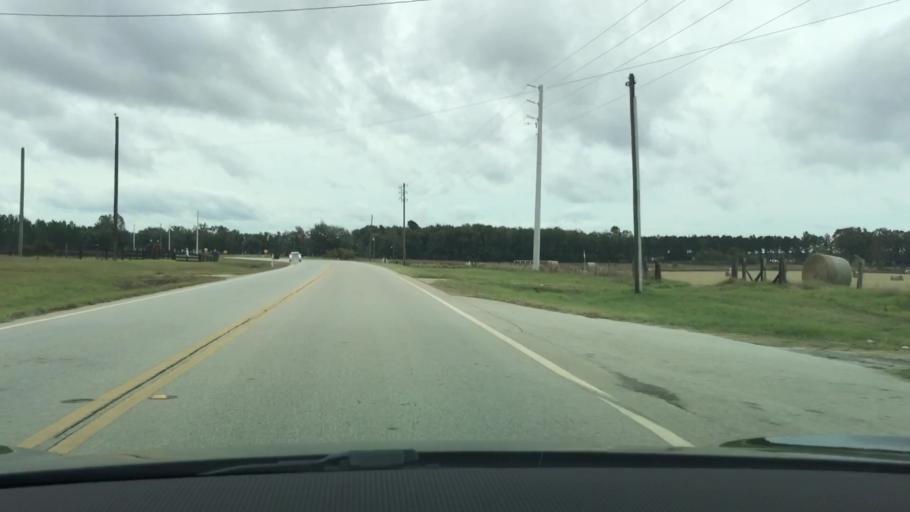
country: US
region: Georgia
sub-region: Jefferson County
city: Wrens
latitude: 33.1621
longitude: -82.4565
